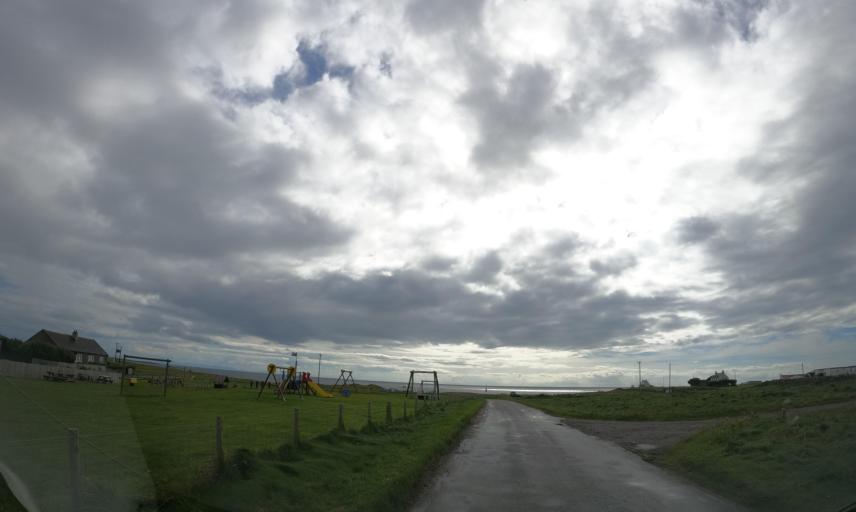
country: GB
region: Scotland
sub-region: Eilean Siar
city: Barra
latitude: 56.4896
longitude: -6.8806
